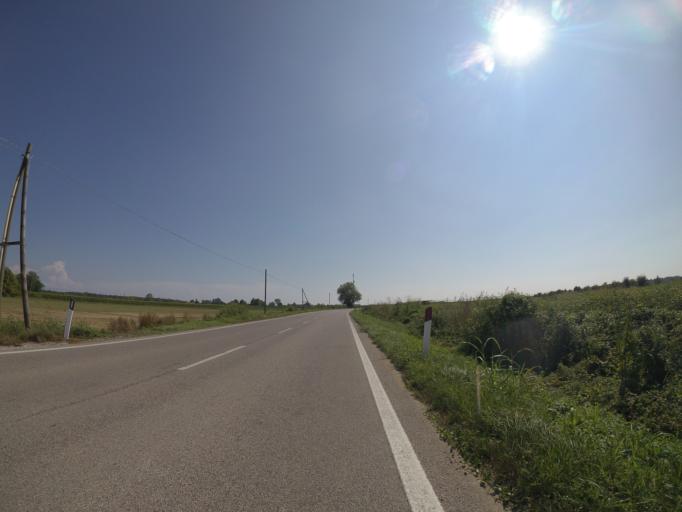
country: IT
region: Friuli Venezia Giulia
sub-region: Provincia di Udine
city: Carlino
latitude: 45.8030
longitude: 13.1657
